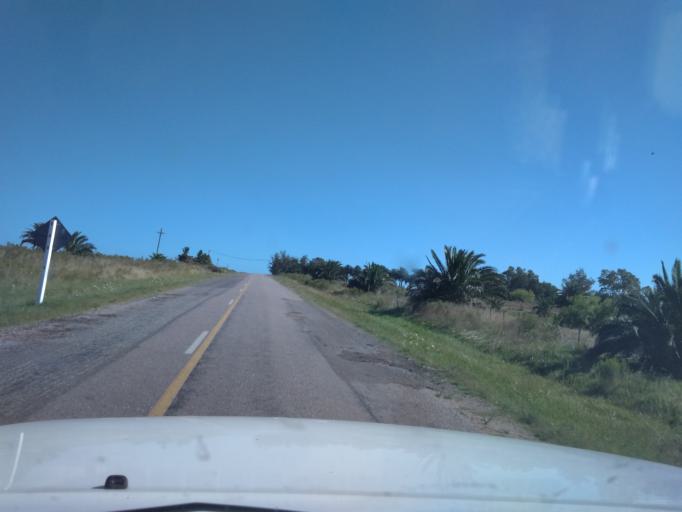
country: UY
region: Canelones
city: San Ramon
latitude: -34.1599
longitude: -55.9470
